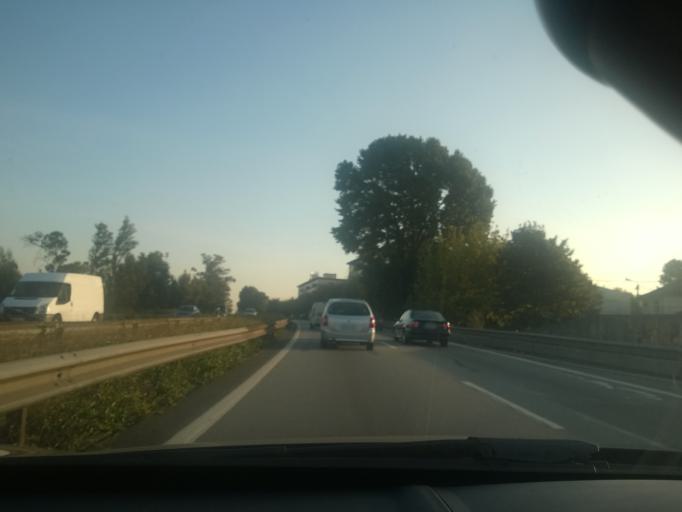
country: PT
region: Porto
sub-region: Matosinhos
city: Senhora da Hora
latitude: 41.1941
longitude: -8.6285
